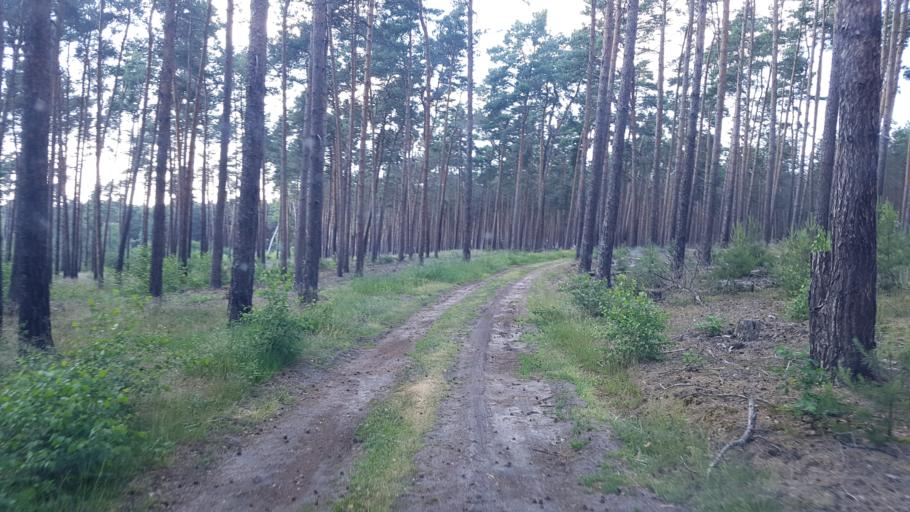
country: DE
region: Brandenburg
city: Trobitz
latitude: 51.6427
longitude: 13.4153
